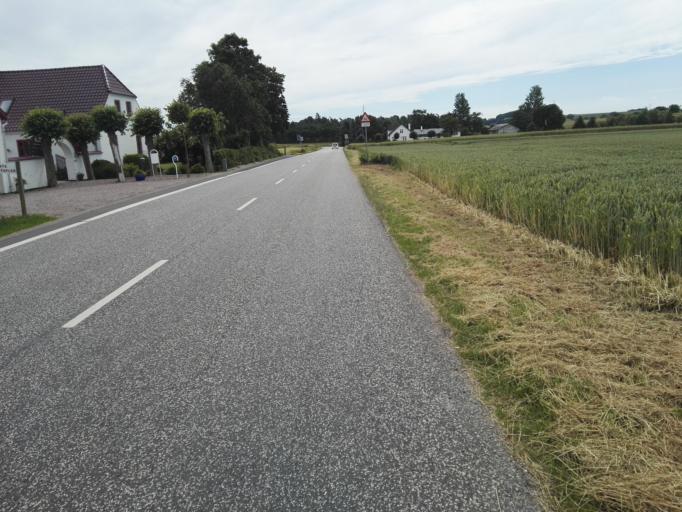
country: DK
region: Capital Region
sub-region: Hillerod Kommune
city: Skaevinge
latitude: 55.9019
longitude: 12.1514
